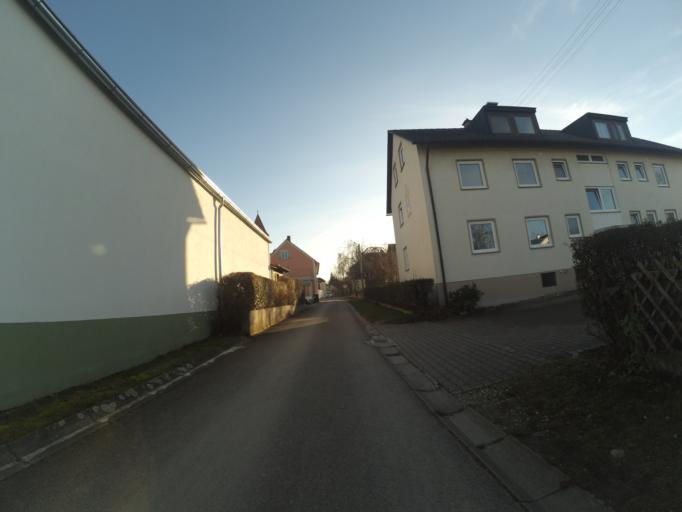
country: DE
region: Bavaria
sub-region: Swabia
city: Wasserburg
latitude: 48.4359
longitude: 10.2968
